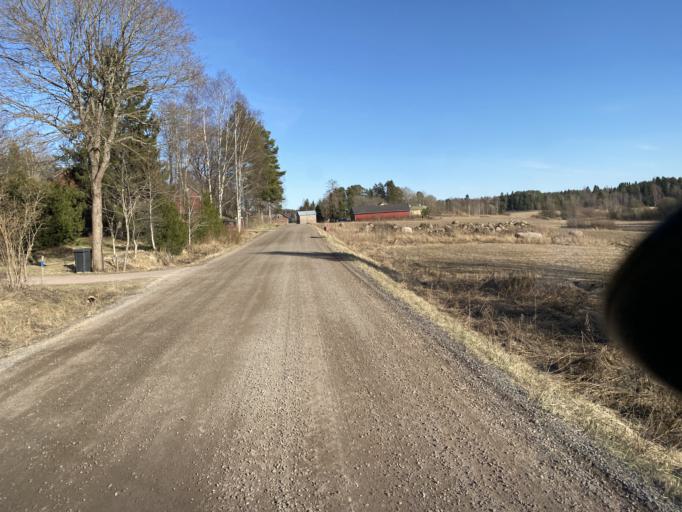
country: FI
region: Satakunta
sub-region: Rauma
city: Lappi
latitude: 61.1413
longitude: 21.9364
